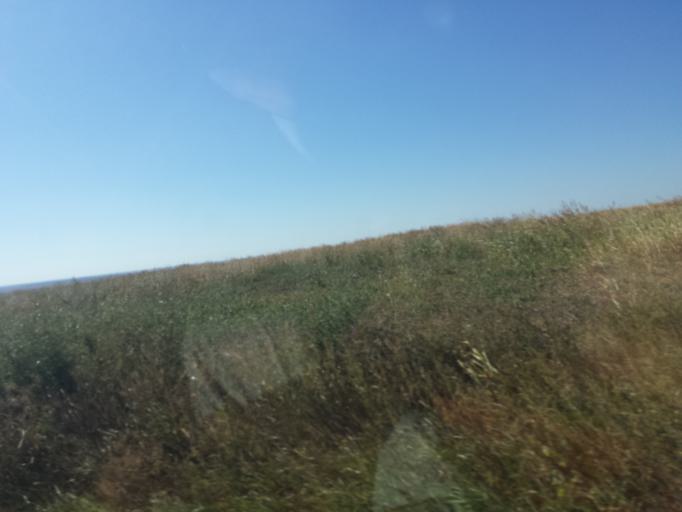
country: RO
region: Constanta
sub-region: Comuna Saraiu
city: Saraiu
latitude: 44.7769
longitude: 28.2251
